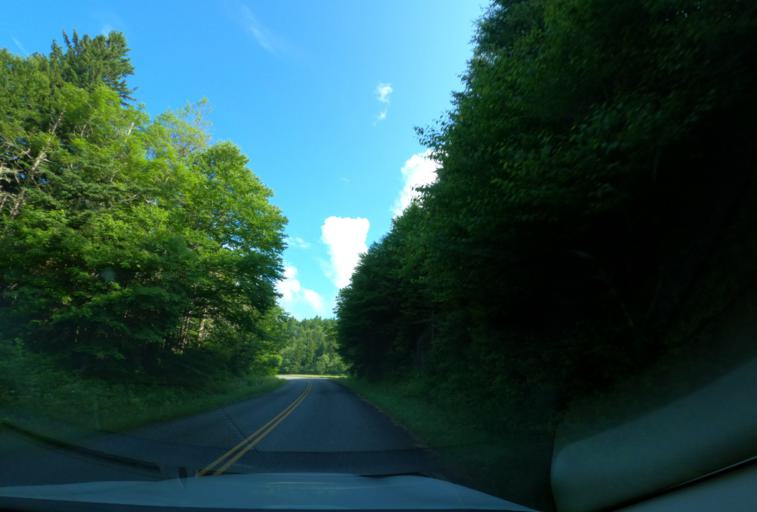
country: US
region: North Carolina
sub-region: Haywood County
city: Hazelwood
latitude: 35.3342
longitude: -82.9659
